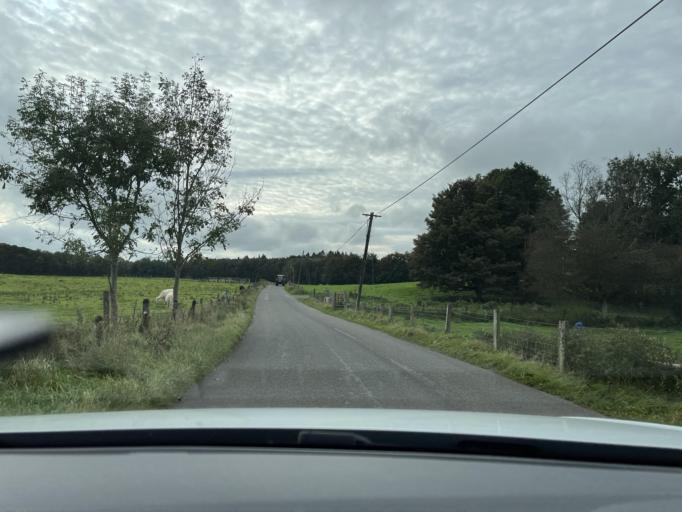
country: IE
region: Connaught
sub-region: Roscommon
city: Boyle
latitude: 53.9784
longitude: -8.2541
